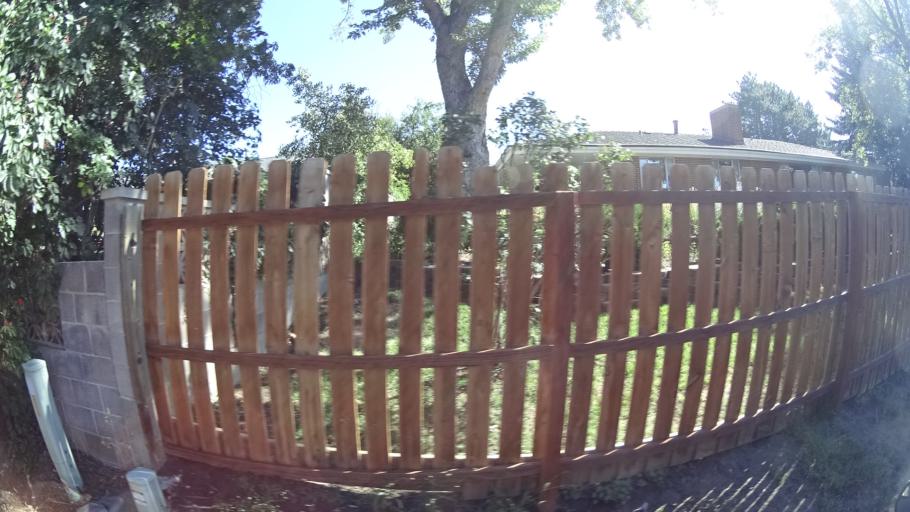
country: US
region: Colorado
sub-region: El Paso County
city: Colorado Springs
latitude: 38.8733
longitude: -104.7827
